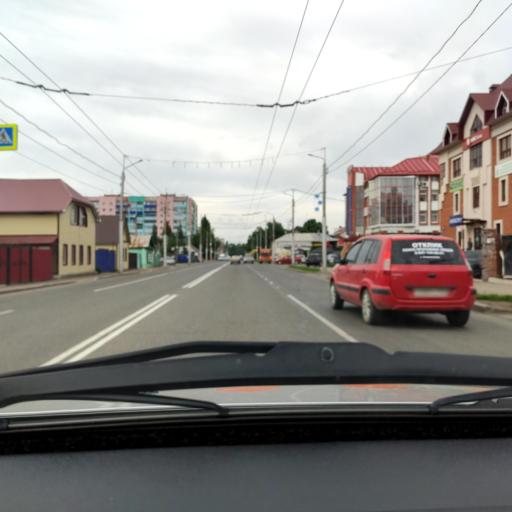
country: RU
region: Bashkortostan
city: Sterlitamak
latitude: 53.6157
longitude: 55.9574
